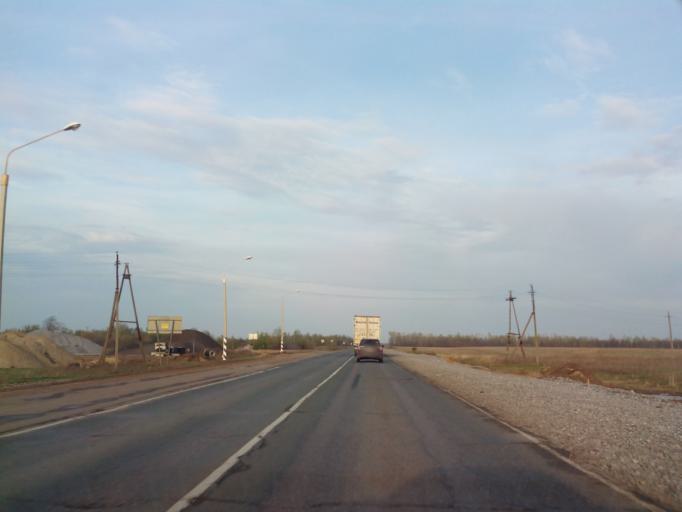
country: RU
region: Rjazan
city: Zarechnyy
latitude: 53.7522
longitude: 39.8185
